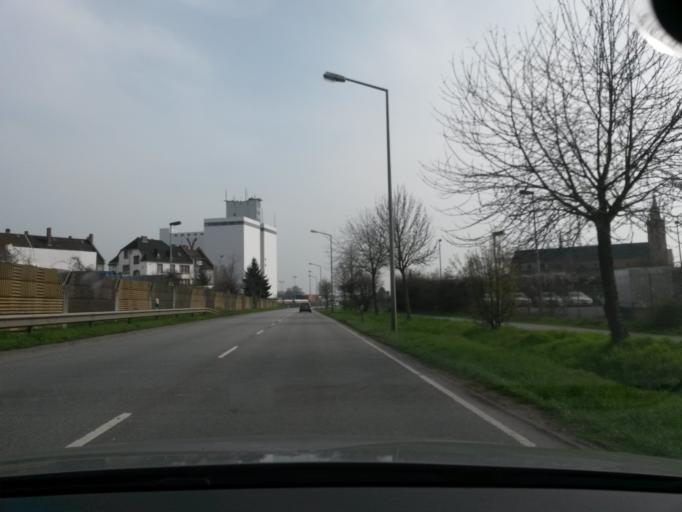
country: DE
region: Rheinland-Pfalz
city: Worms
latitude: 49.6422
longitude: 8.3689
